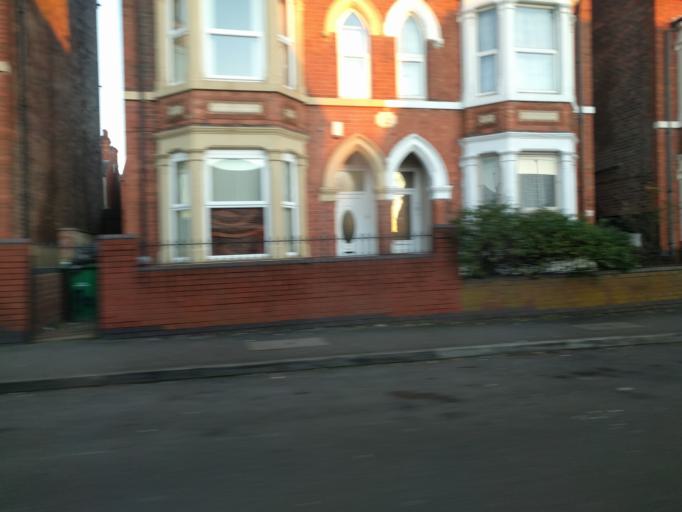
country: GB
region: England
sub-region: Nottingham
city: Nottingham
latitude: 52.9679
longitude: -1.1688
